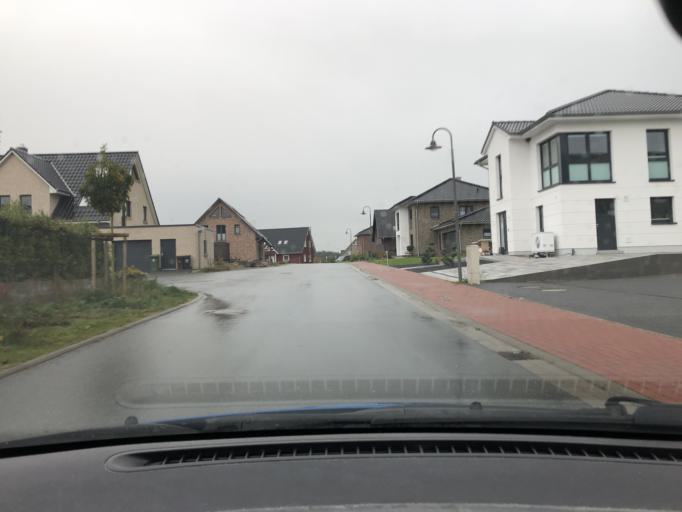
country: DE
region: Schleswig-Holstein
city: Fahrdorf
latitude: 54.5050
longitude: 9.6136
